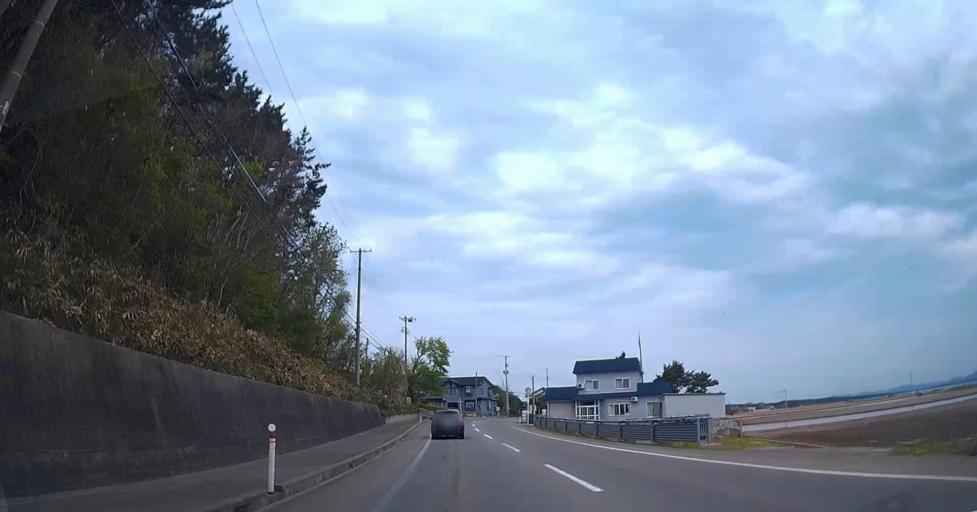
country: JP
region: Aomori
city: Shimokizukuri
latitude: 40.9975
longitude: 140.3474
